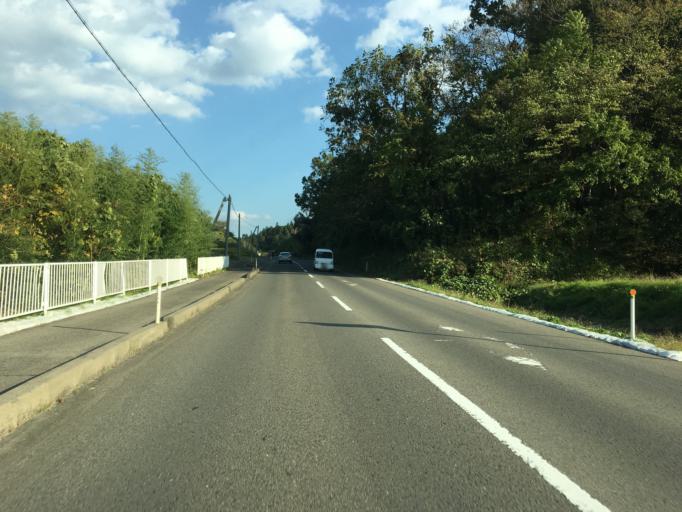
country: JP
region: Fukushima
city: Fukushima-shi
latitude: 37.6702
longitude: 140.5218
